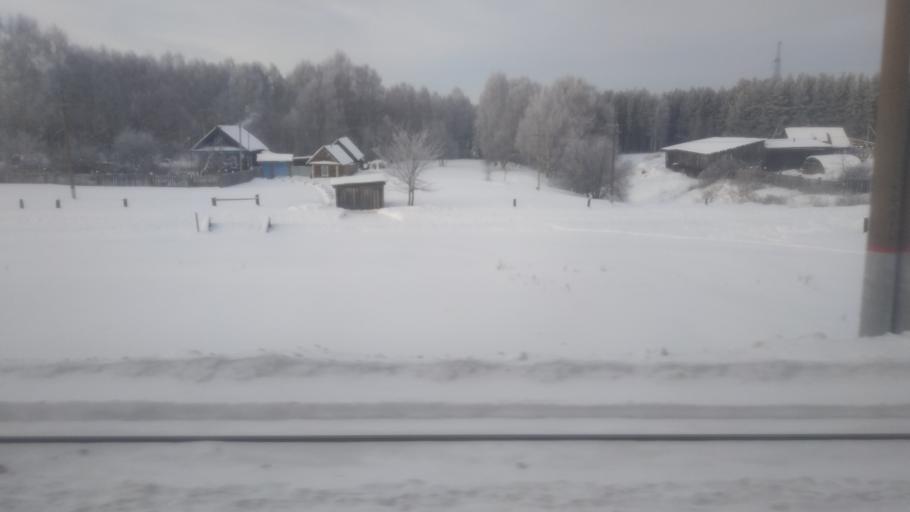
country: RU
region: Udmurtiya
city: Kizner
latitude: 56.3867
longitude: 51.7160
